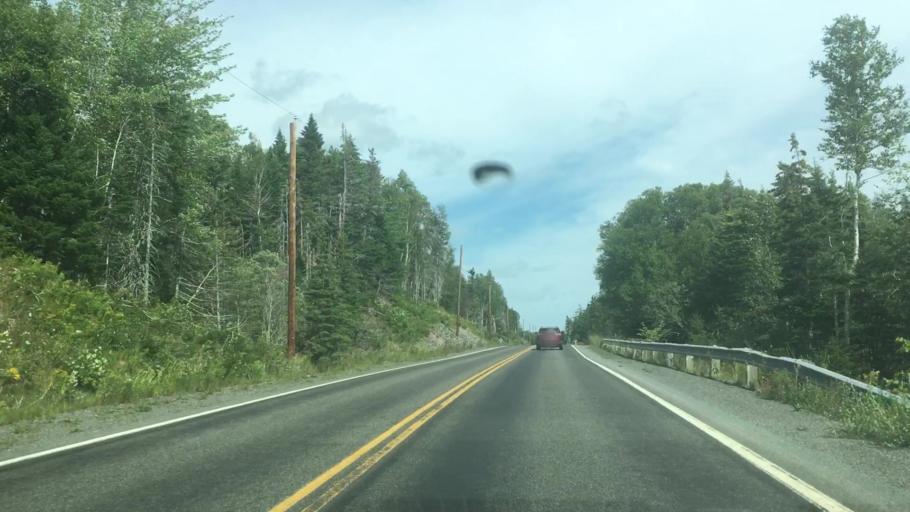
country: CA
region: Nova Scotia
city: Sydney Mines
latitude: 46.2087
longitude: -60.6224
